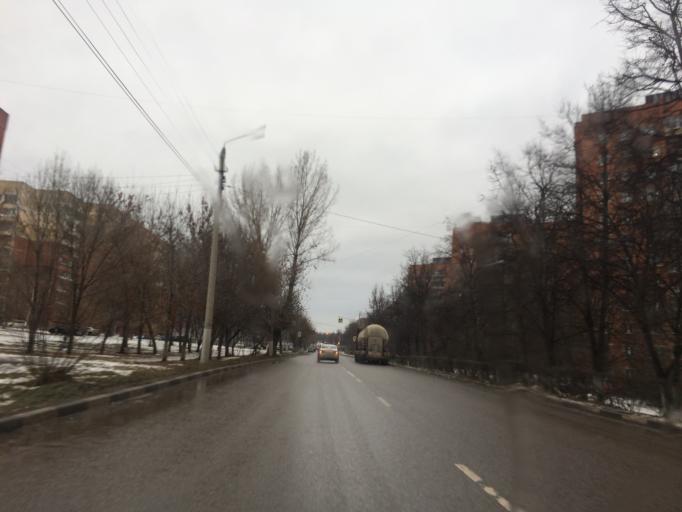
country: RU
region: Tula
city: Tula
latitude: 54.1963
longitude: 37.6456
